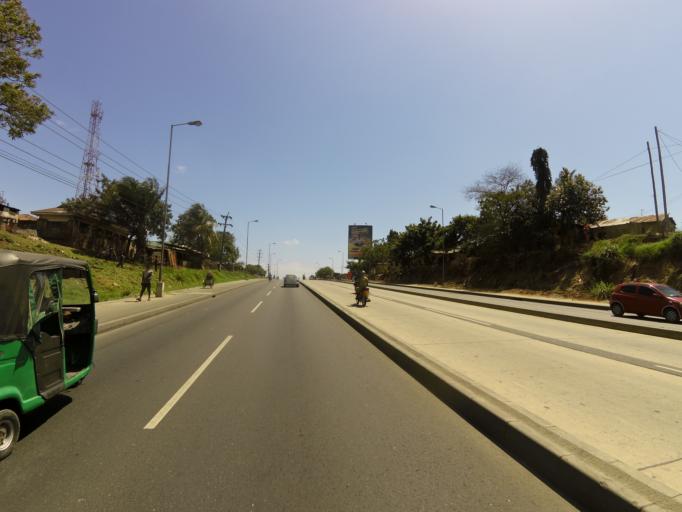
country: TZ
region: Dar es Salaam
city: Magomeni
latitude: -6.7986
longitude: 39.2631
